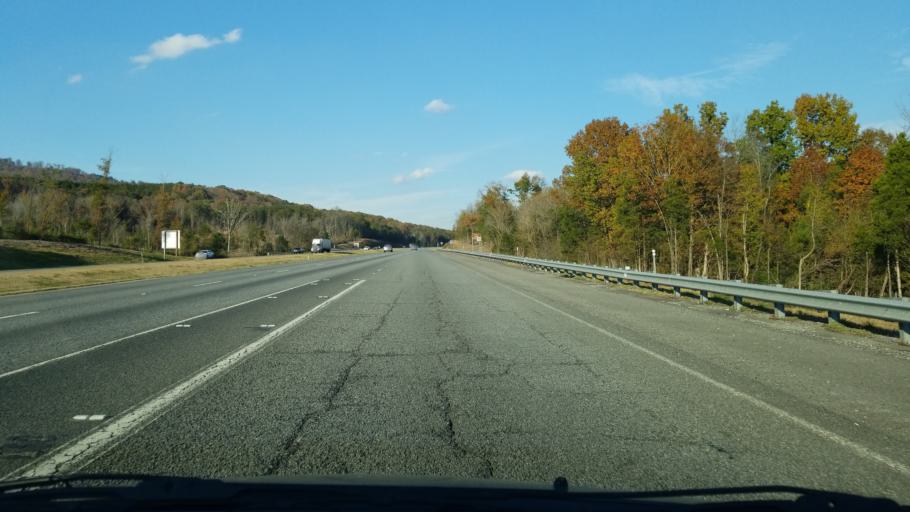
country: US
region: Georgia
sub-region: Dade County
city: Trenton
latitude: 34.8729
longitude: -85.5146
